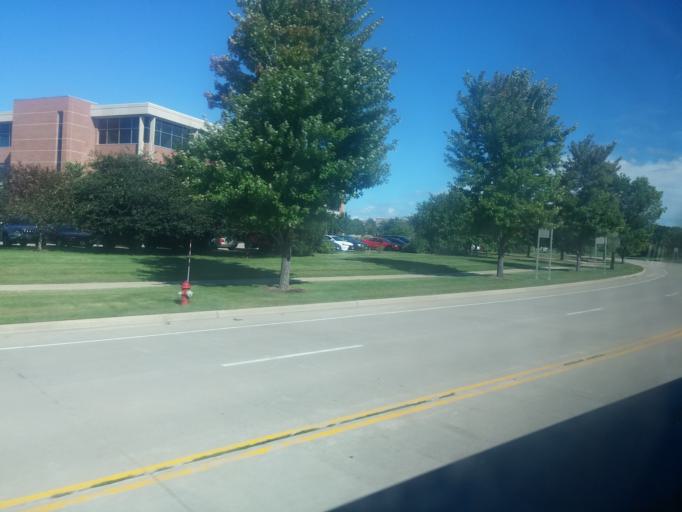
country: US
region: Wisconsin
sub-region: Dane County
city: Windsor
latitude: 43.1446
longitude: -89.2961
